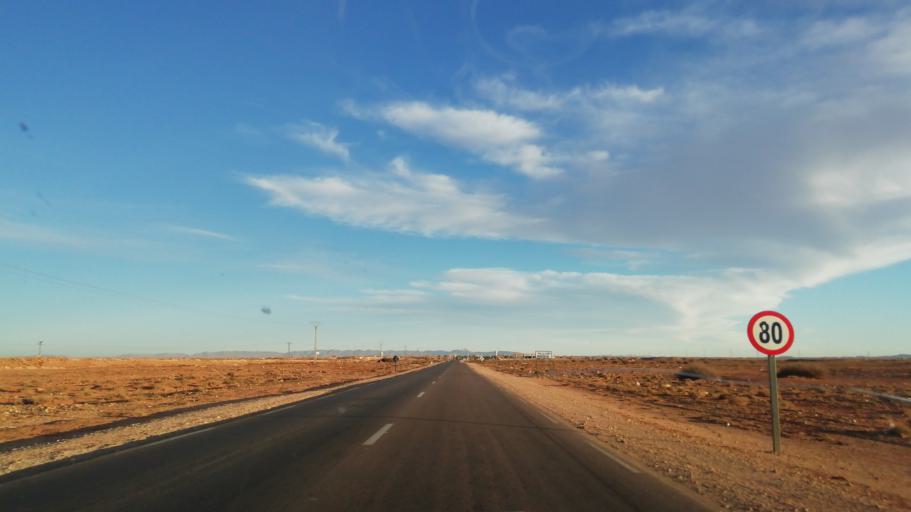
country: DZ
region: Wilaya de Naama
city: Naama
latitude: 33.7294
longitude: -0.7501
